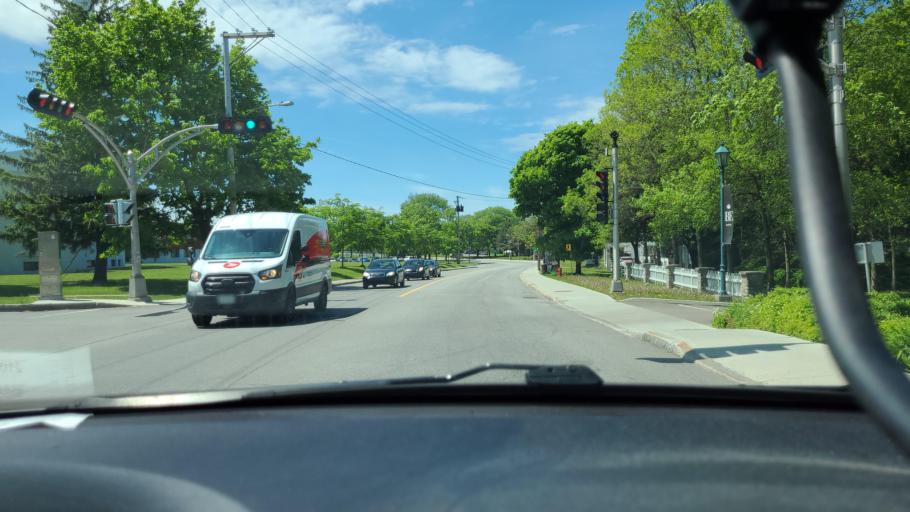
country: CA
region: Quebec
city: L'Ancienne-Lorette
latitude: 46.7681
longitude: -71.3232
